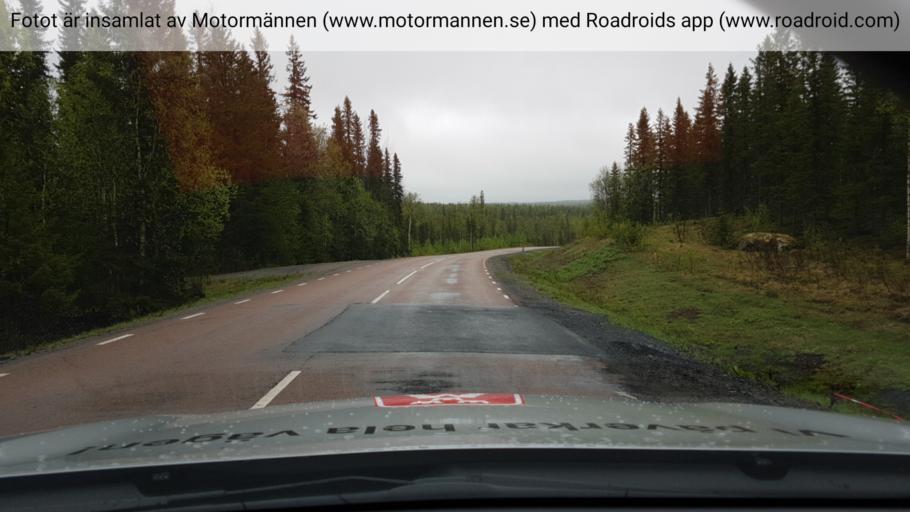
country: SE
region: Jaemtland
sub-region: Krokoms Kommun
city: Valla
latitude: 63.1525
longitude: 13.9598
